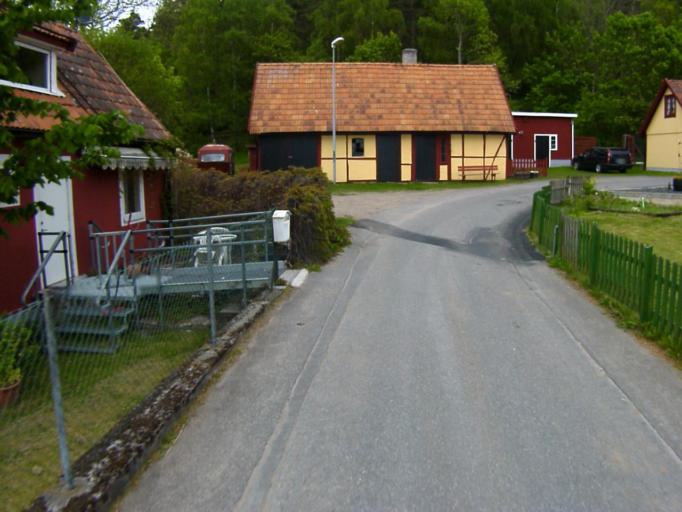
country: SE
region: Skane
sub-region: Kristianstads Kommun
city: Degeberga
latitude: 55.8362
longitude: 14.0945
